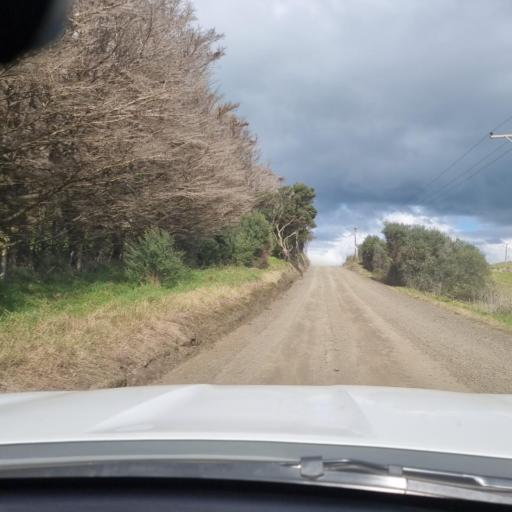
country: NZ
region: Auckland
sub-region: Auckland
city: Wellsford
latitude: -36.3557
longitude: 174.1746
